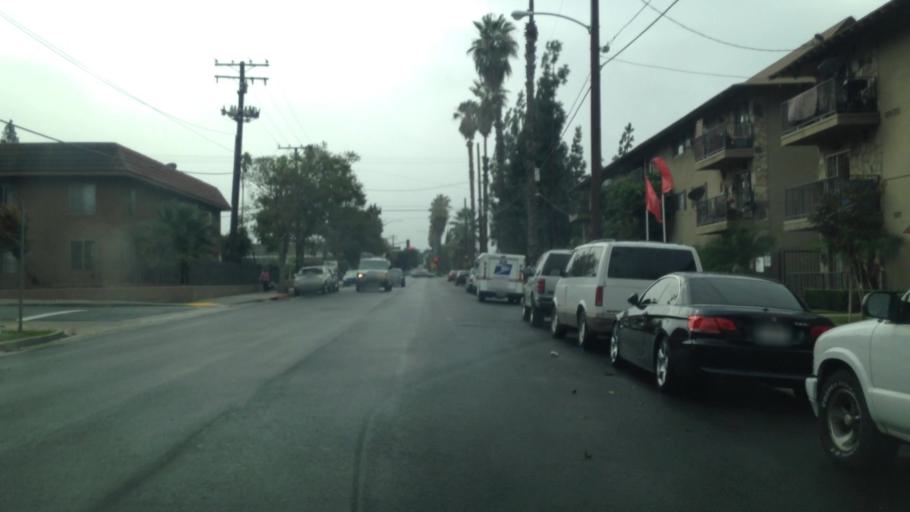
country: US
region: California
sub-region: Riverside County
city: Highgrove
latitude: 33.9774
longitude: -117.3442
